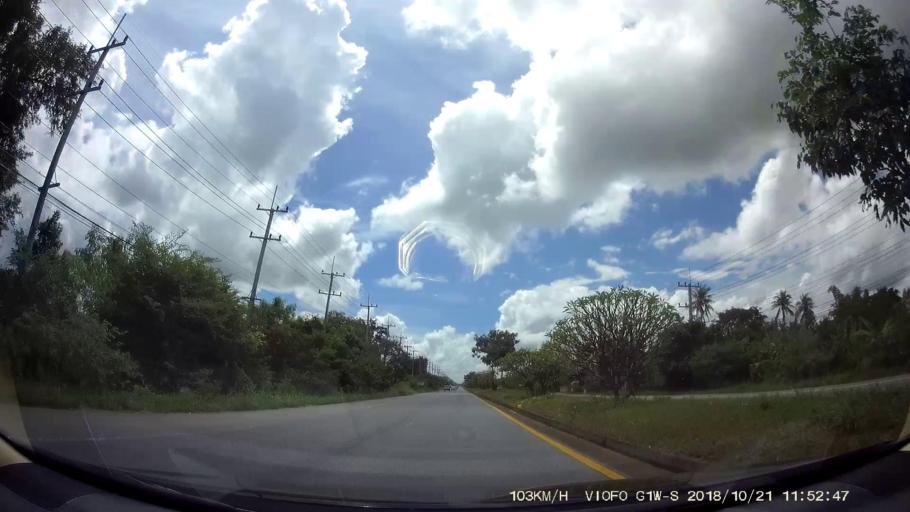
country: TH
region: Chaiyaphum
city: Chatturat
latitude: 15.6044
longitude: 101.9096
